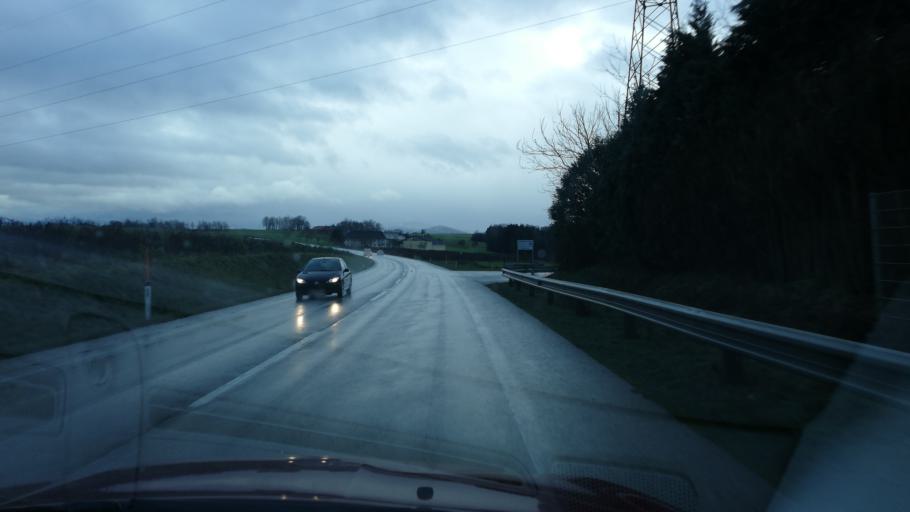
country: AT
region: Upper Austria
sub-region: Wels-Land
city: Sattledt
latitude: 48.0008
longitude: 14.0660
